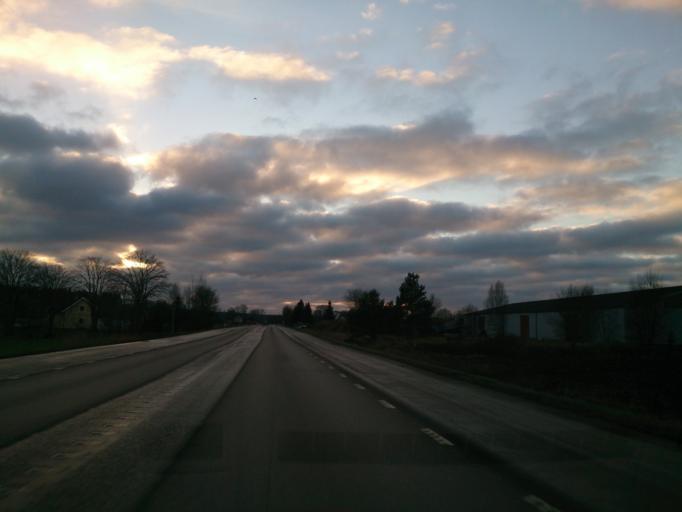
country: SE
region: OEstergoetland
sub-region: Norrkopings Kommun
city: Kimstad
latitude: 58.4708
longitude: 15.8989
